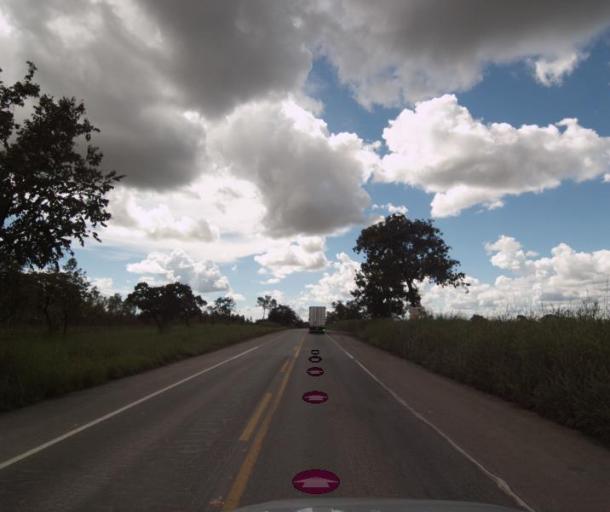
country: BR
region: Goias
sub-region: Porangatu
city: Porangatu
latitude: -13.5084
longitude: -49.1248
